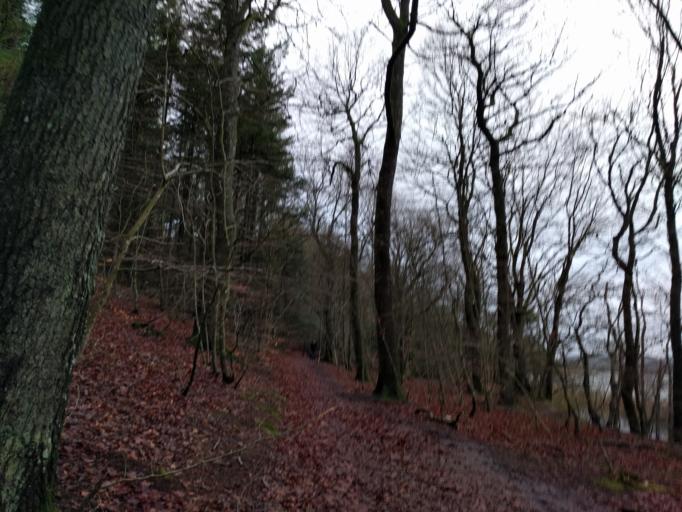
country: DK
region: Central Jutland
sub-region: Silkeborg Kommune
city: Silkeborg
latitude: 56.1673
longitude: 9.5218
